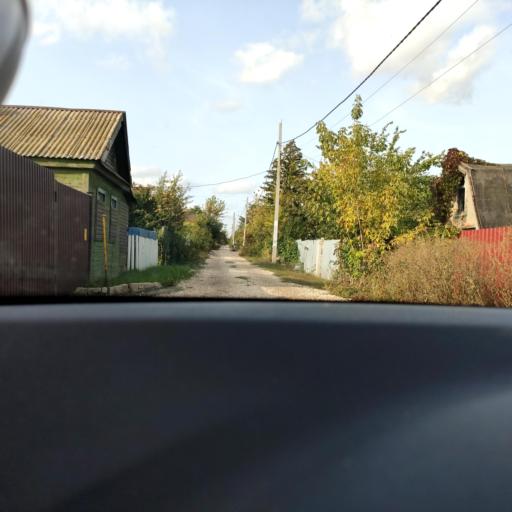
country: RU
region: Samara
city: Petra-Dubrava
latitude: 53.2776
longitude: 50.2965
